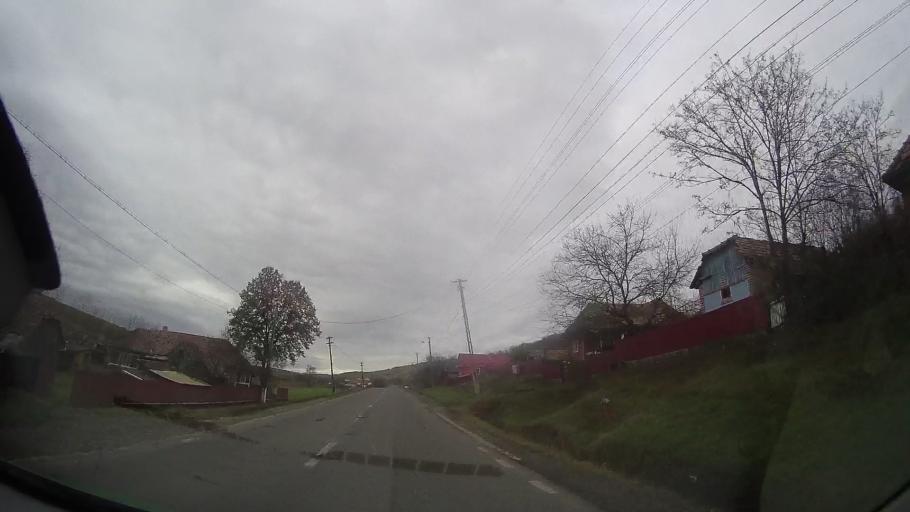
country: RO
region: Mures
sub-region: Comuna Craesti
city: Craiesti
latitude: 46.7579
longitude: 24.4105
